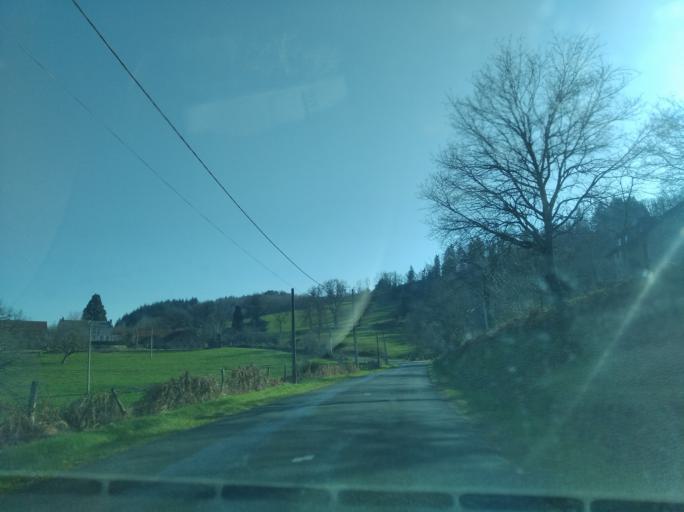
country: FR
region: Auvergne
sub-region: Departement de l'Allier
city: Le Mayet-de-Montagne
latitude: 46.1100
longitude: 3.6868
